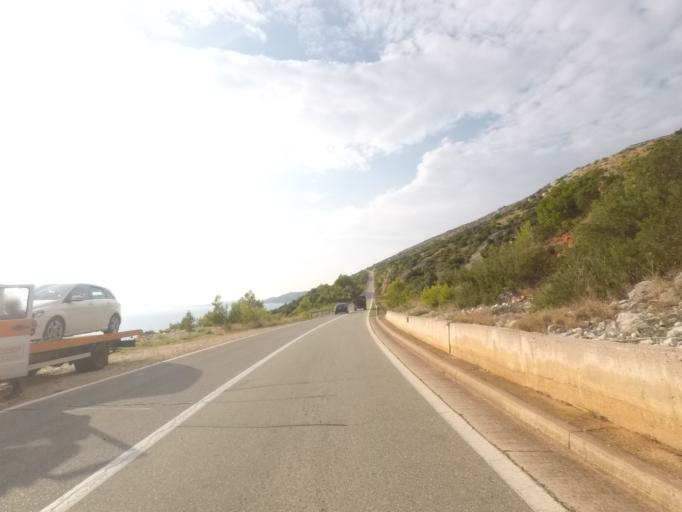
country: HR
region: Splitsko-Dalmatinska
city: Stari Grad
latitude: 43.1483
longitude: 16.5240
